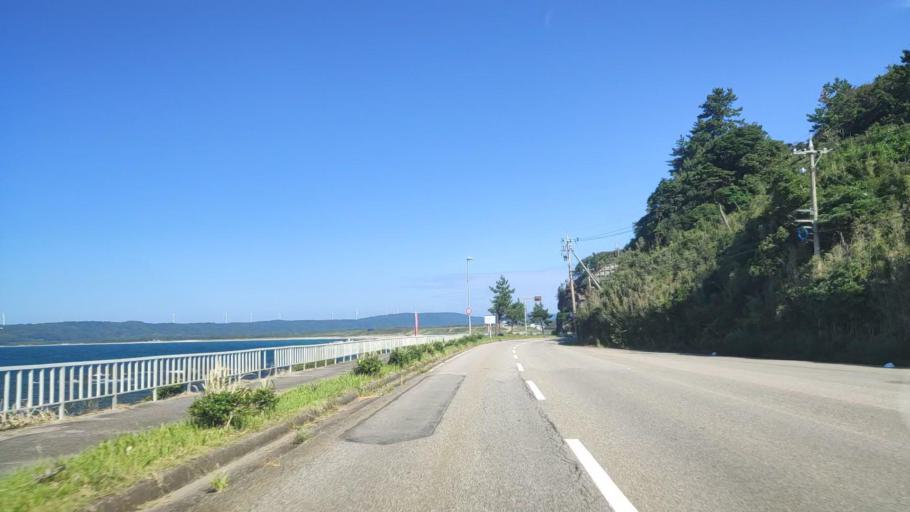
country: JP
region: Ishikawa
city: Nanao
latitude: 37.1296
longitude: 136.7272
